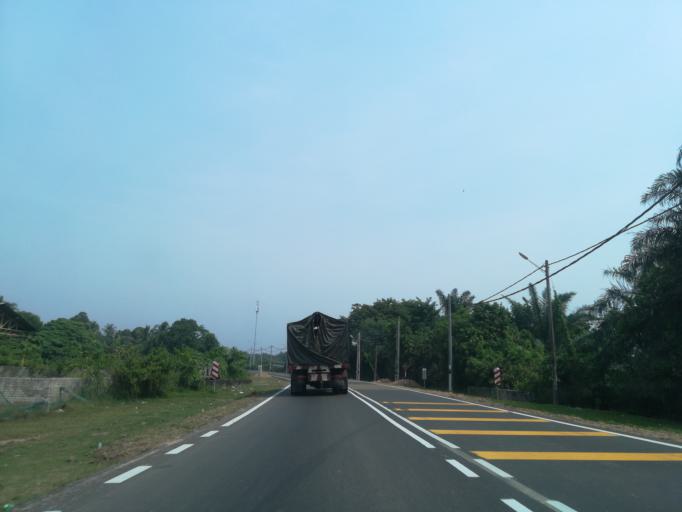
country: MY
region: Penang
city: Tasek Glugor
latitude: 5.4623
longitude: 100.5466
